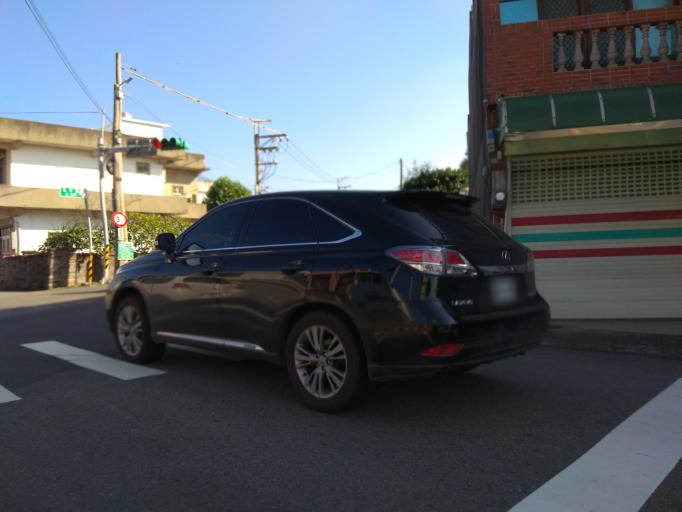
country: TW
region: Taiwan
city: Taoyuan City
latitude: 25.0362
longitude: 121.1170
